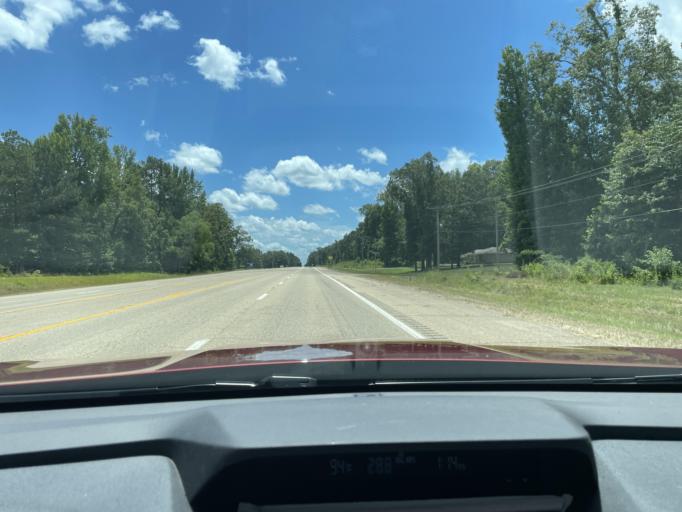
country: US
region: Arkansas
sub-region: Drew County
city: Monticello
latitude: 33.6629
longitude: -91.8035
